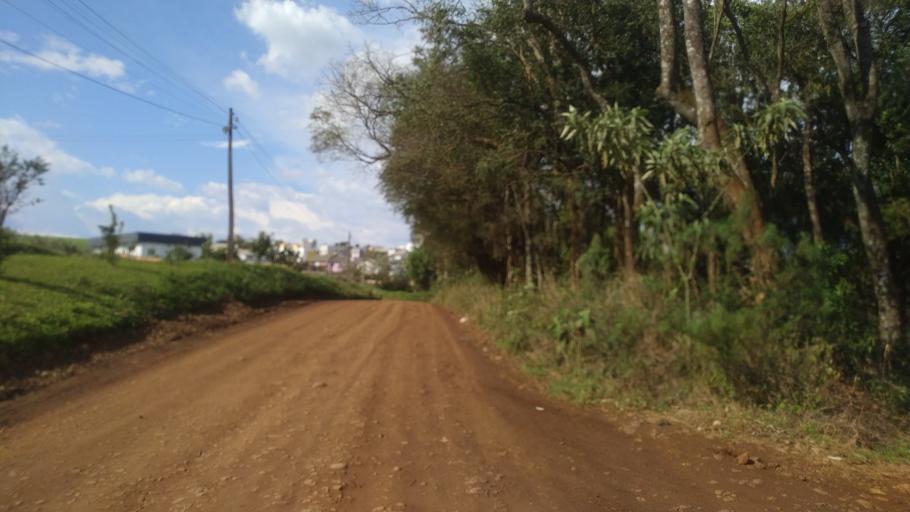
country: BR
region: Santa Catarina
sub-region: Chapeco
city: Chapeco
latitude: -27.0866
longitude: -52.7167
